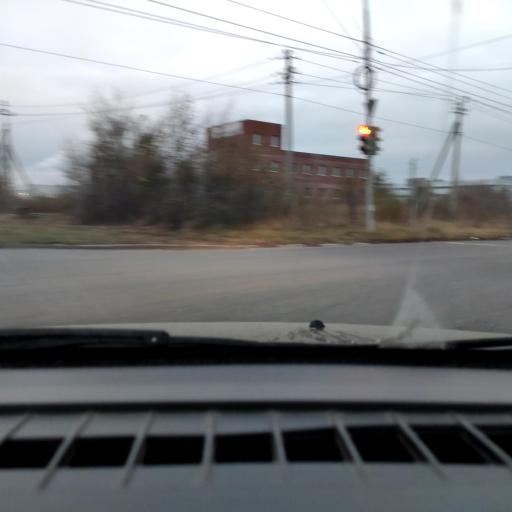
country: RU
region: Samara
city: Tol'yatti
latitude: 53.5608
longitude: 49.2952
